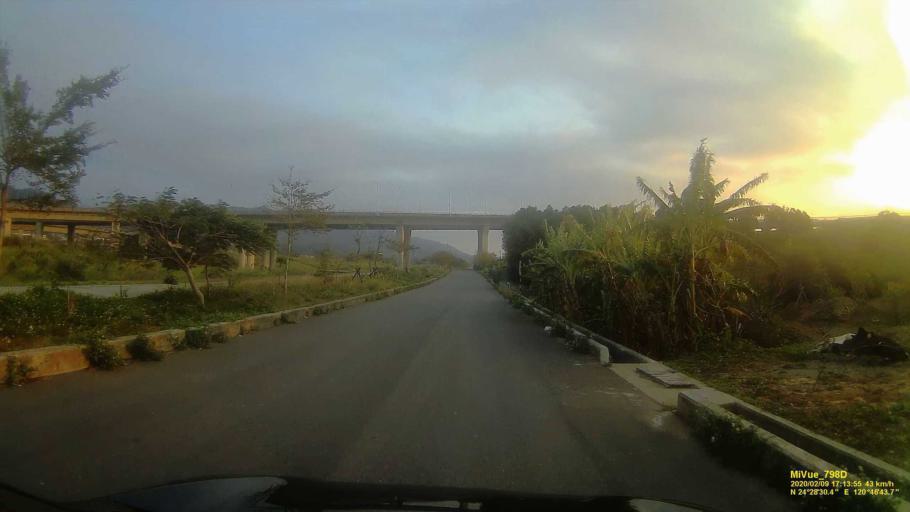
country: TW
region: Taiwan
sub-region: Miaoli
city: Miaoli
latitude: 24.4750
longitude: 120.7788
